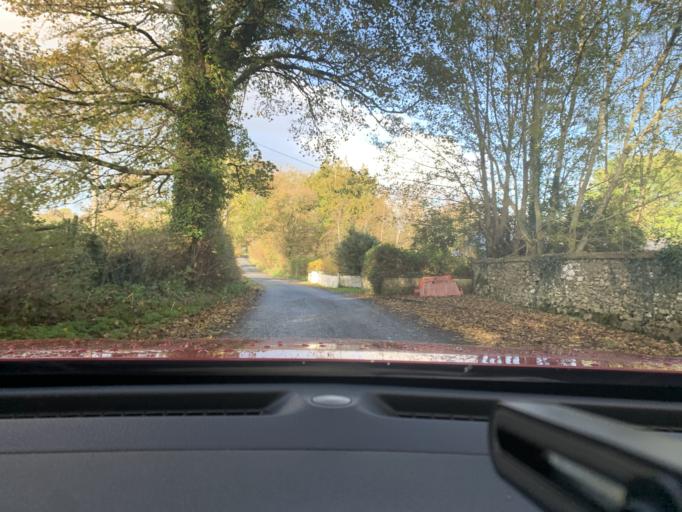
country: IE
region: Connaught
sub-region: Sligo
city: Ballymote
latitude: 54.0987
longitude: -8.4358
